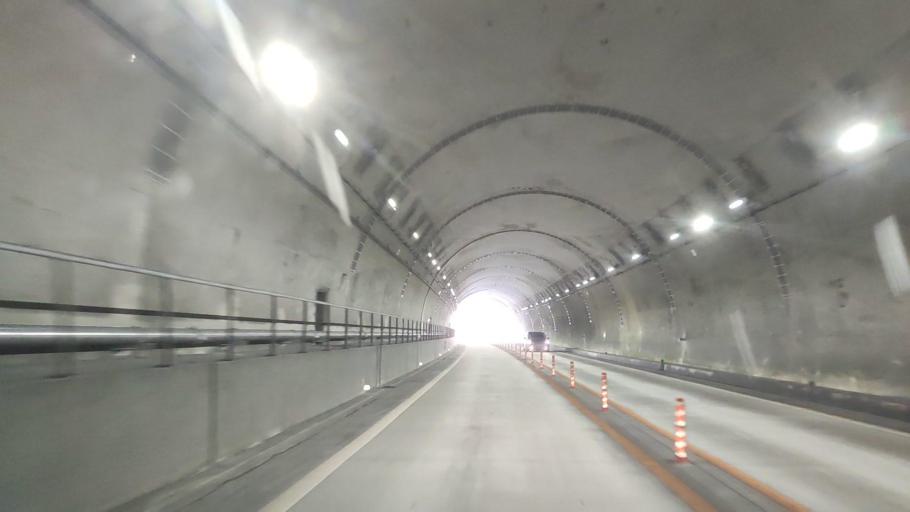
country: JP
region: Ehime
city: Hojo
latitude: 34.0867
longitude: 132.9782
